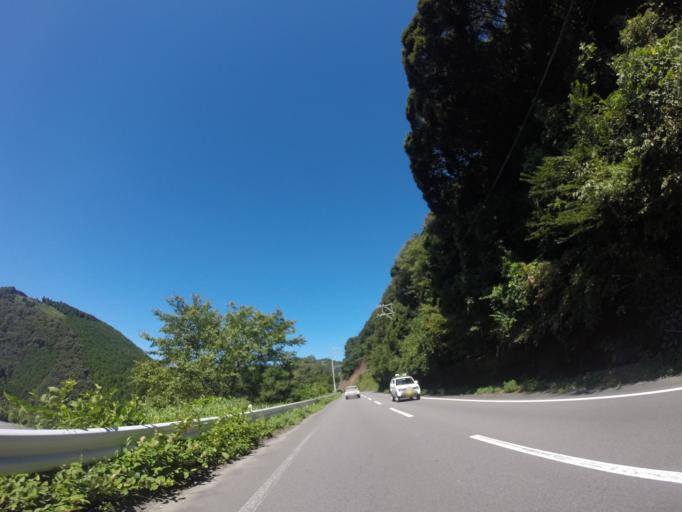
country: JP
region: Shizuoka
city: Kanaya
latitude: 34.8937
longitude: 138.1168
